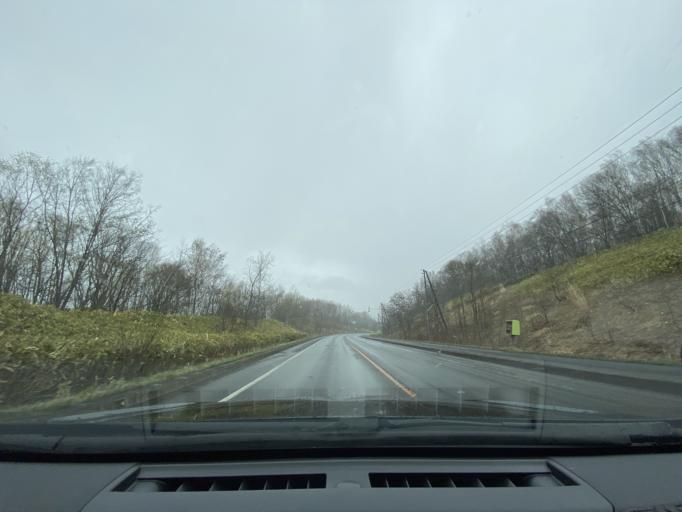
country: JP
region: Hokkaido
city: Fukagawa
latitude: 43.7147
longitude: 142.1741
